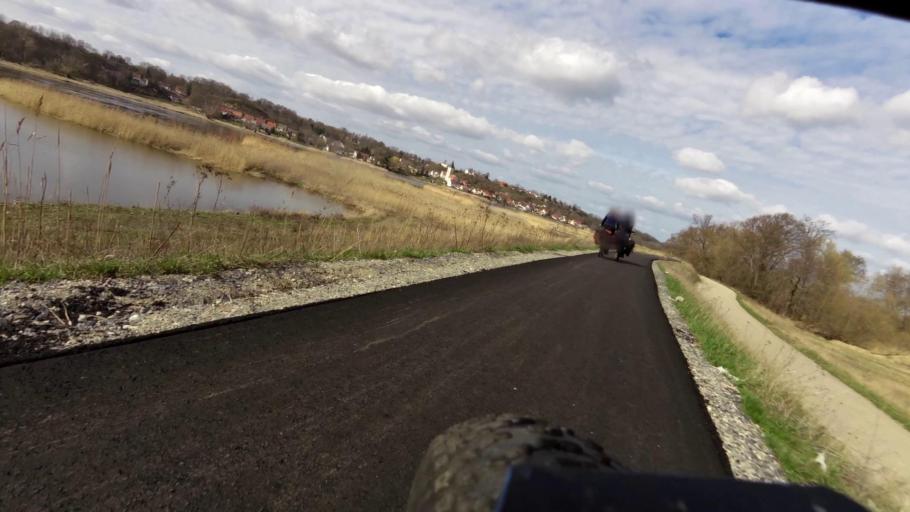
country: DE
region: Brandenburg
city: Lebus
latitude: 52.4201
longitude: 14.5478
